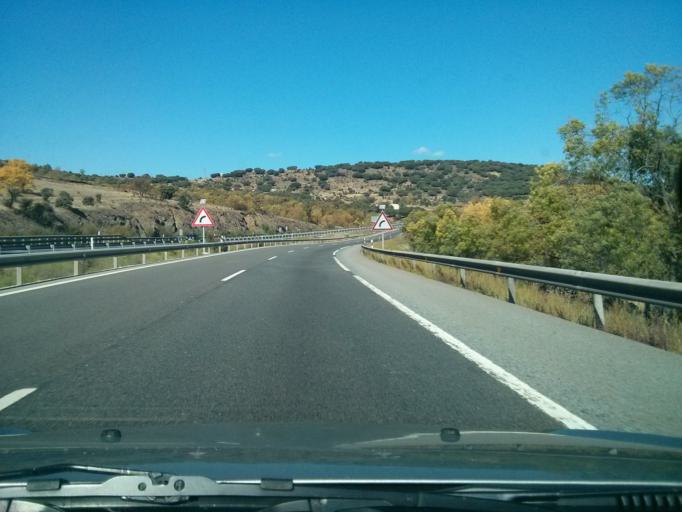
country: ES
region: Madrid
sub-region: Provincia de Madrid
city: Buitrago del Lozoya
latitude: 40.9450
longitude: -3.6362
